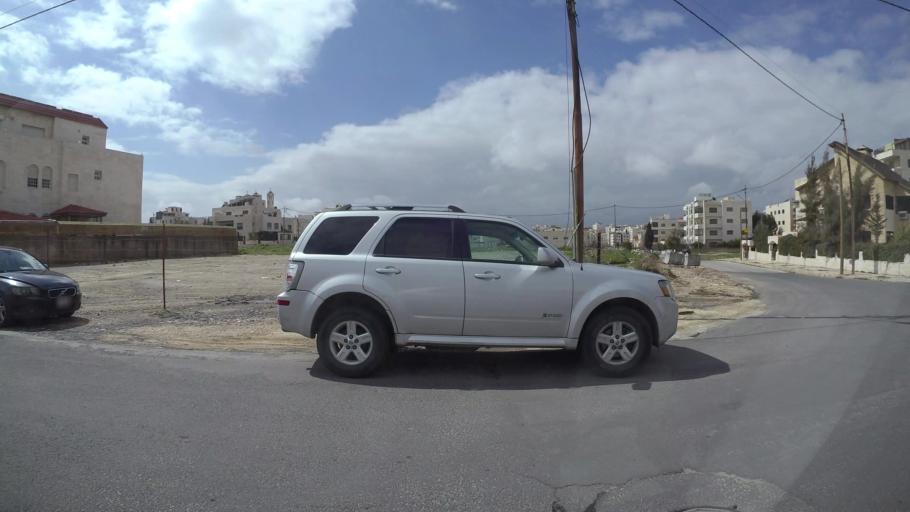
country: JO
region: Amman
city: Al Jubayhah
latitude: 31.9931
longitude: 35.8452
